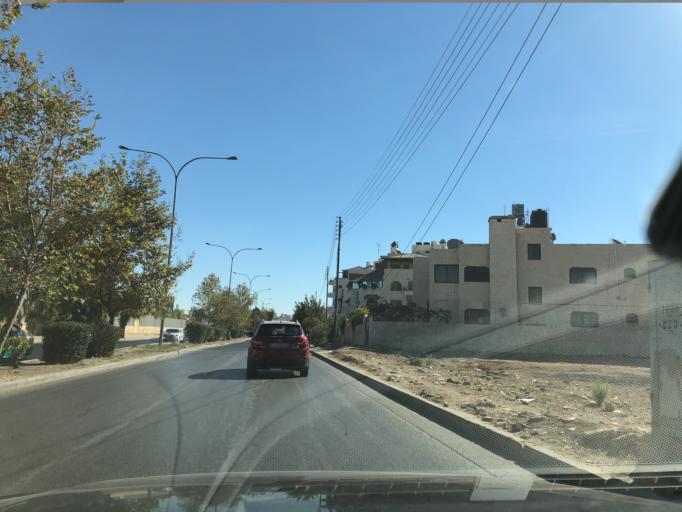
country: JO
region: Amman
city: Wadi as Sir
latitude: 31.9687
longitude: 35.8345
